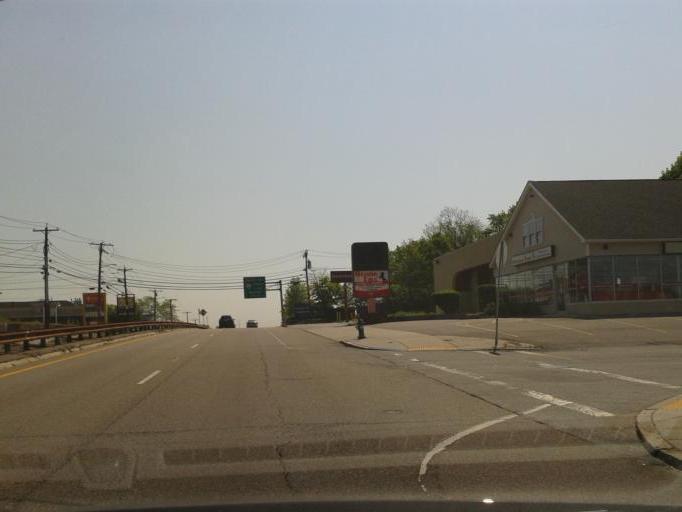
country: US
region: Massachusetts
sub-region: Middlesex County
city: Framingham
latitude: 42.2984
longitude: -71.4047
